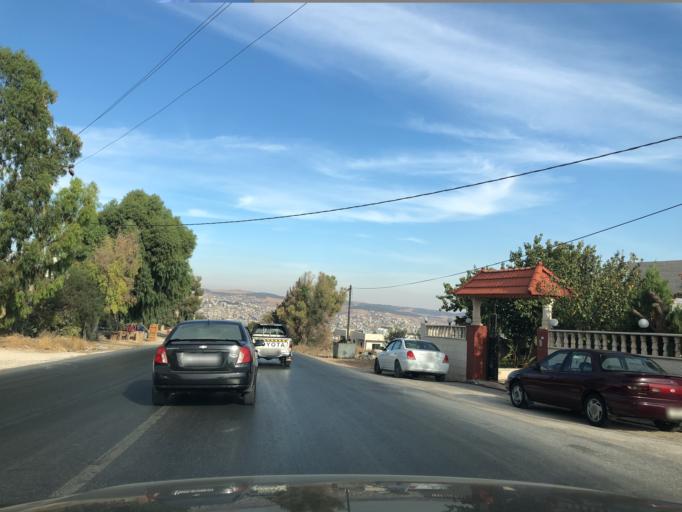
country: JO
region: Irbid
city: Al Kittah
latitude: 32.2807
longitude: 35.8611
